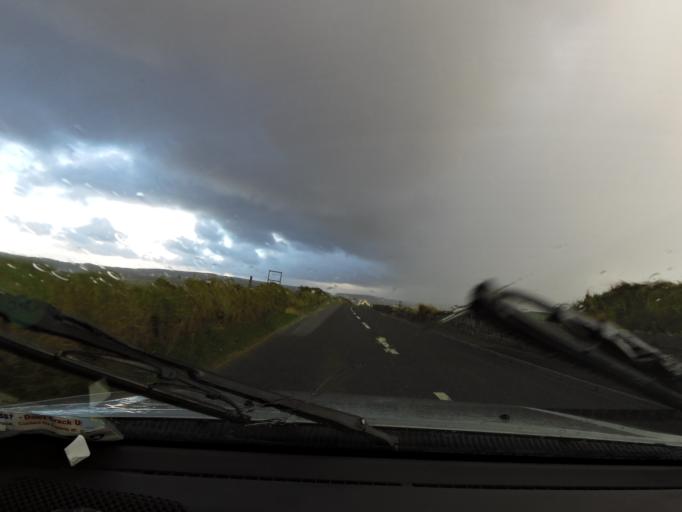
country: IE
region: Munster
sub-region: An Clar
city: Kilrush
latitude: 52.9460
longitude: -9.3516
